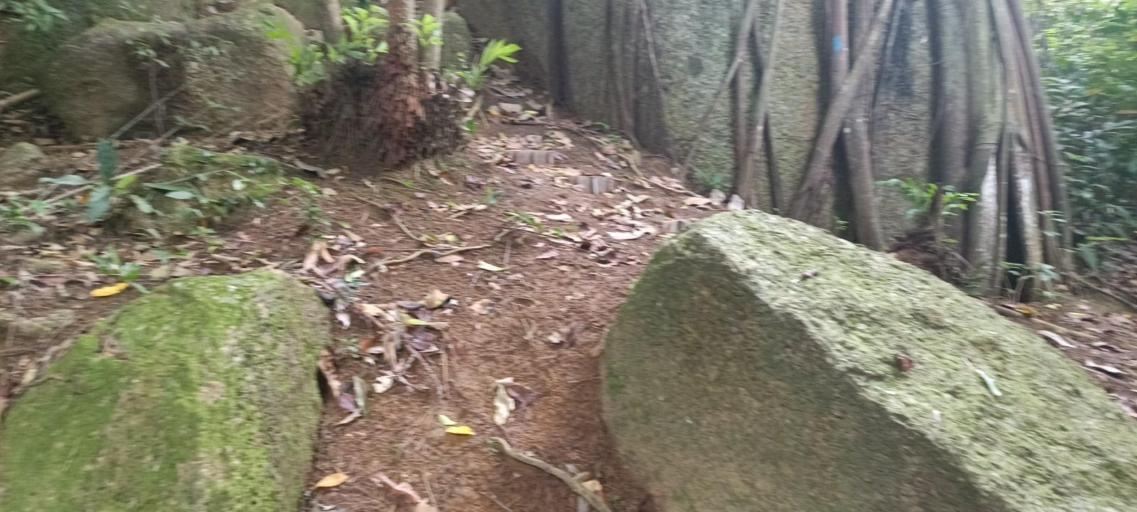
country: MY
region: Penang
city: Kampung Sungai Ara
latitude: 5.2614
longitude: 100.2742
